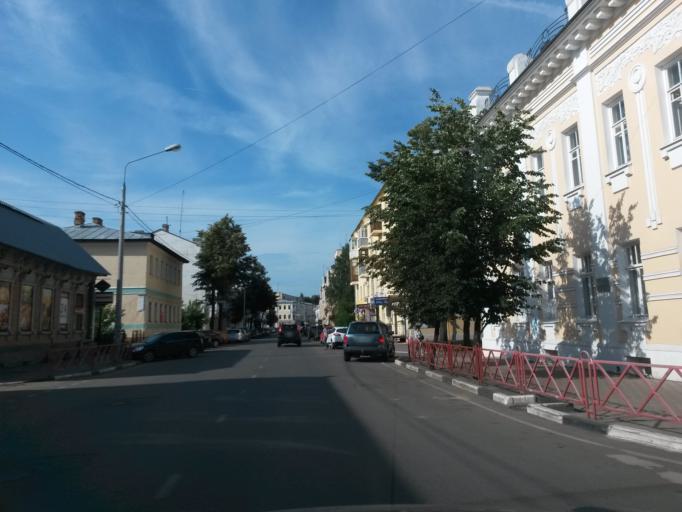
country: RU
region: Jaroslavl
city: Yaroslavl
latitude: 57.6232
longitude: 39.8817
